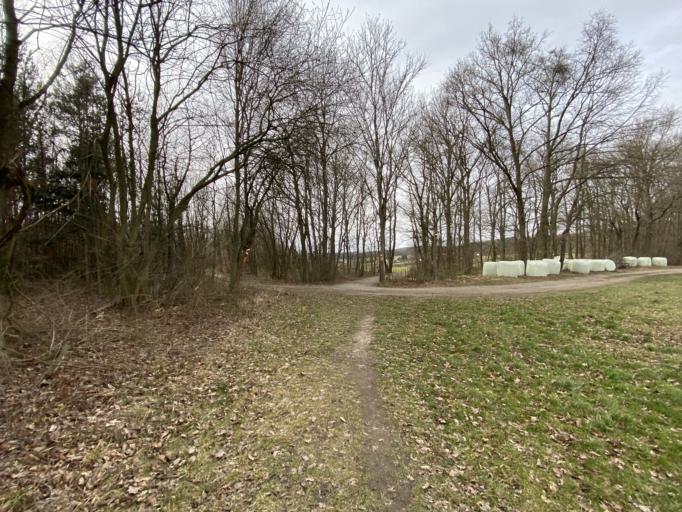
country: AT
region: Lower Austria
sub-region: Politischer Bezirk Modling
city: Gaaden
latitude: 48.0344
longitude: 16.1906
